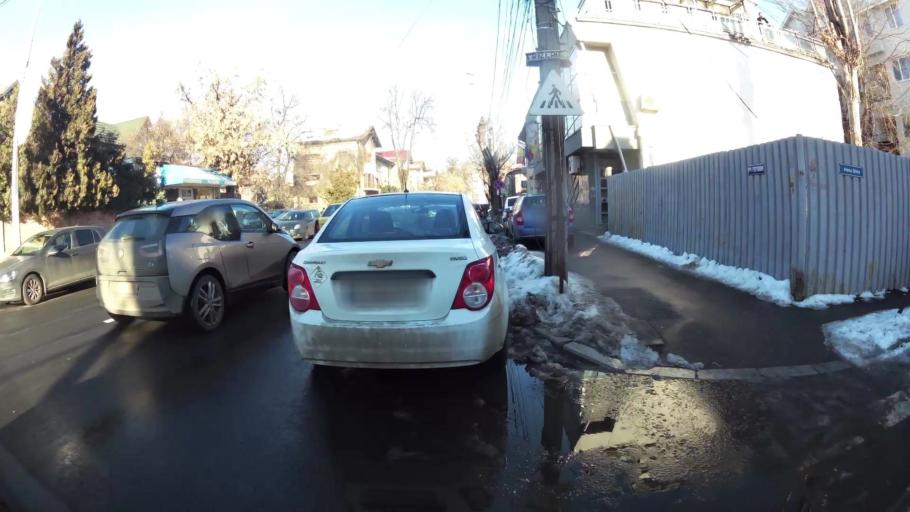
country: RO
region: Bucuresti
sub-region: Municipiul Bucuresti
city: Bucuresti
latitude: 44.4028
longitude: 26.0934
